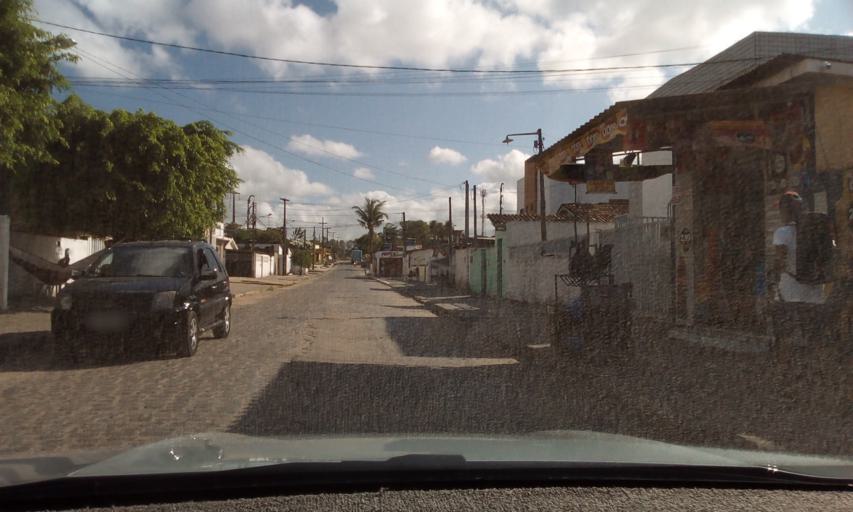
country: BR
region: Paraiba
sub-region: Bayeux
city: Bayeux
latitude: -7.1663
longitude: -34.9074
